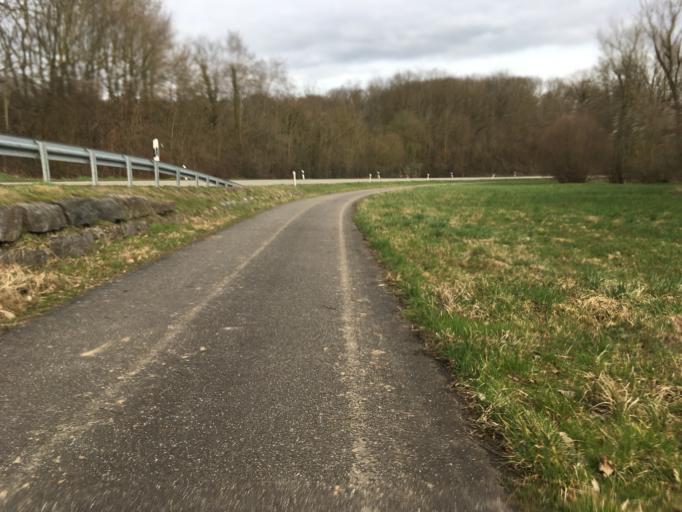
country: DE
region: Baden-Wuerttemberg
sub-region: Regierungsbezirk Stuttgart
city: Bretzfeld
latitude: 49.2067
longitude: 9.4261
